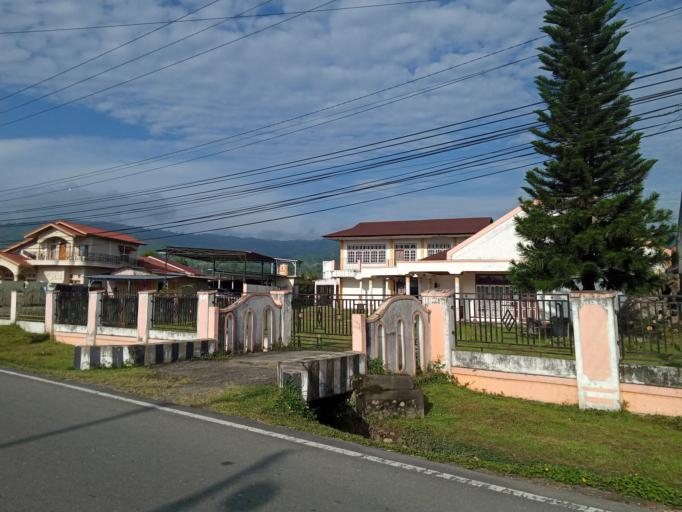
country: ID
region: Jambi
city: Semurup
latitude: -2.0053
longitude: 101.3767
